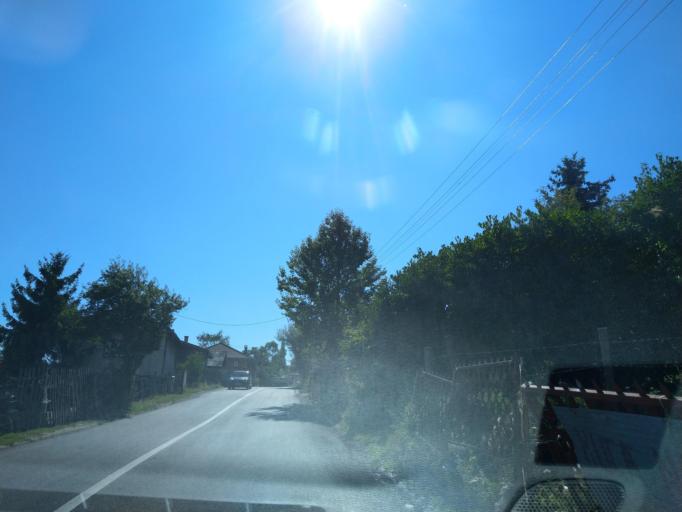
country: RS
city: Sokolovica
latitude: 43.2515
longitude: 20.2280
